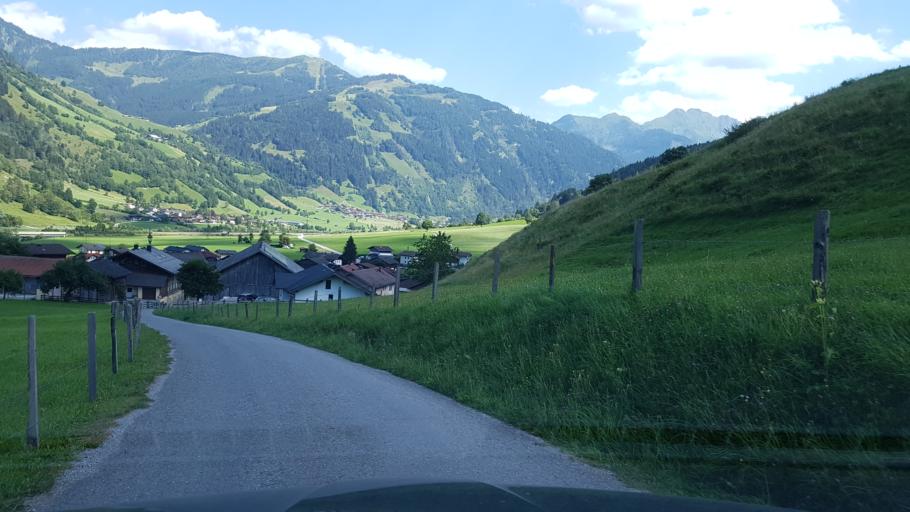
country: AT
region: Salzburg
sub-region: Politischer Bezirk Sankt Johann im Pongau
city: Dorfgastein
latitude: 47.2577
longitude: 13.0801
